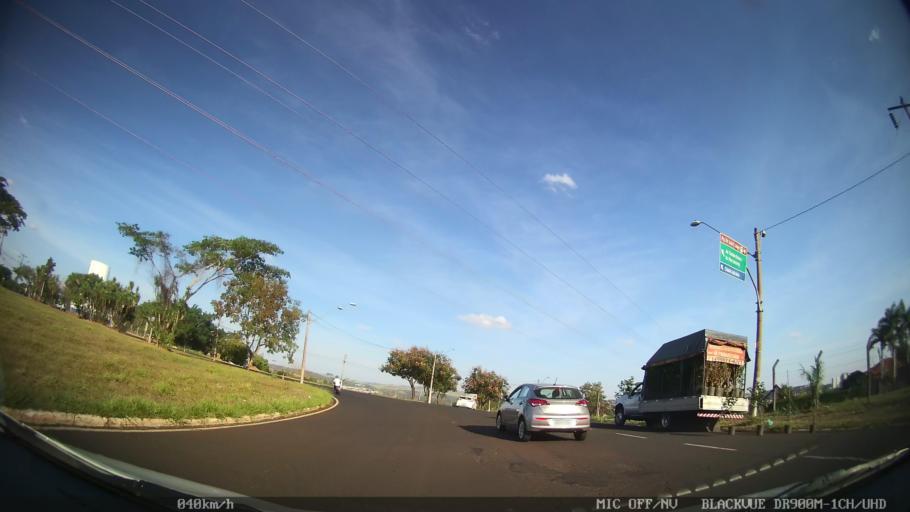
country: BR
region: Sao Paulo
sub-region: Ribeirao Preto
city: Ribeirao Preto
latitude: -21.2029
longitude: -47.7820
